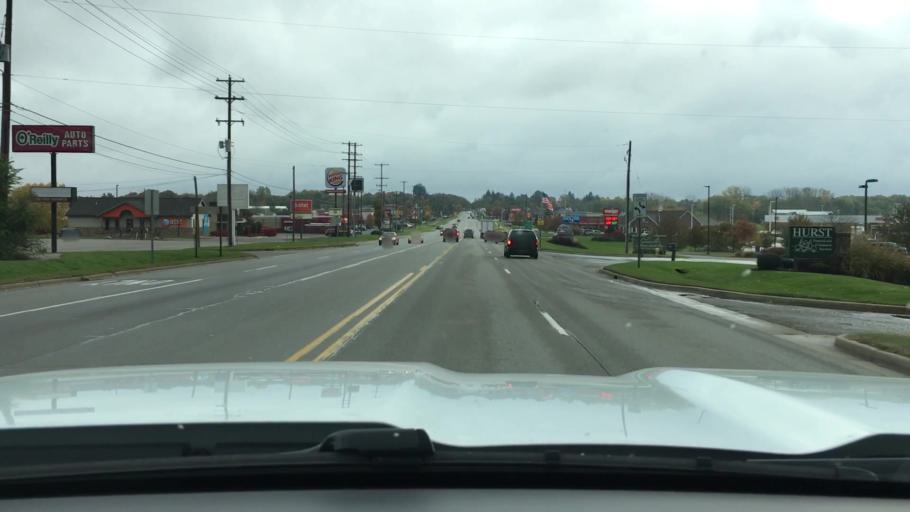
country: US
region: Michigan
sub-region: Montcalm County
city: Greenville
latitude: 43.1771
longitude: -85.2822
